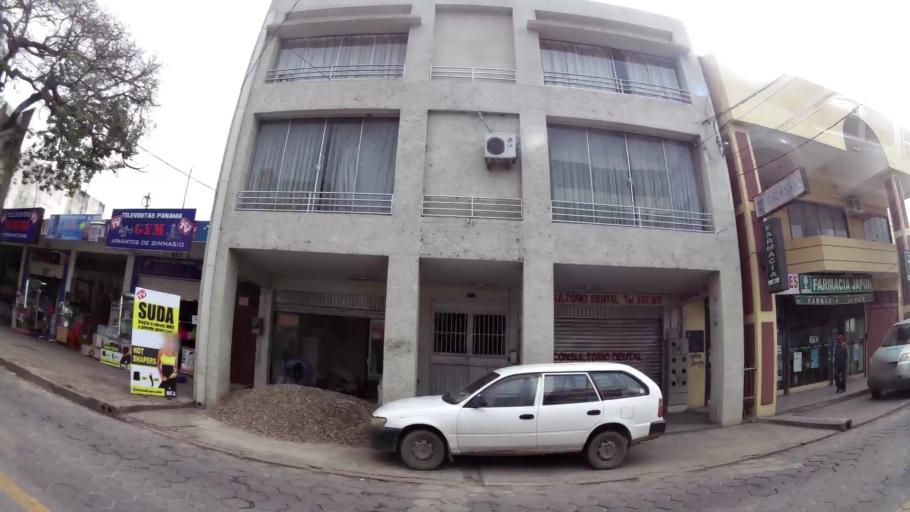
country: BO
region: Santa Cruz
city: Santa Cruz de la Sierra
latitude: -17.7766
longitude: -63.1797
